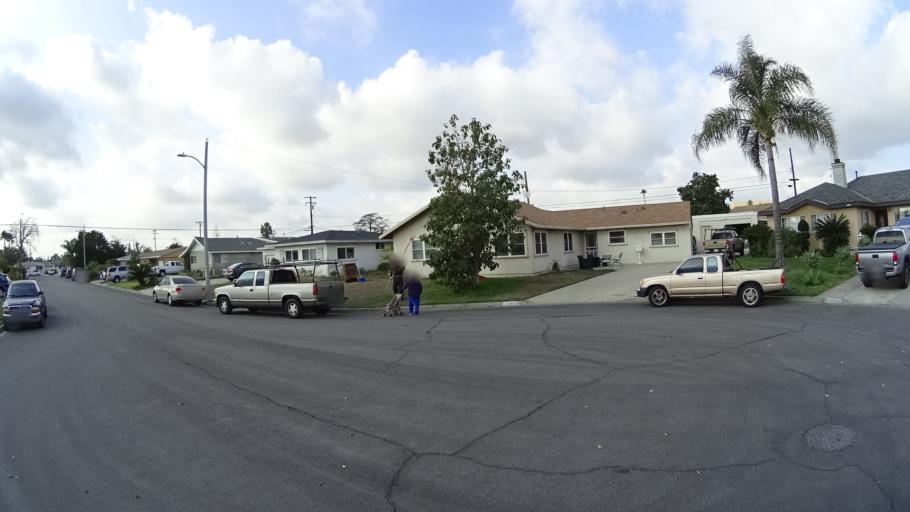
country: US
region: California
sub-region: Orange County
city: Garden Grove
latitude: 33.7719
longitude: -117.9142
